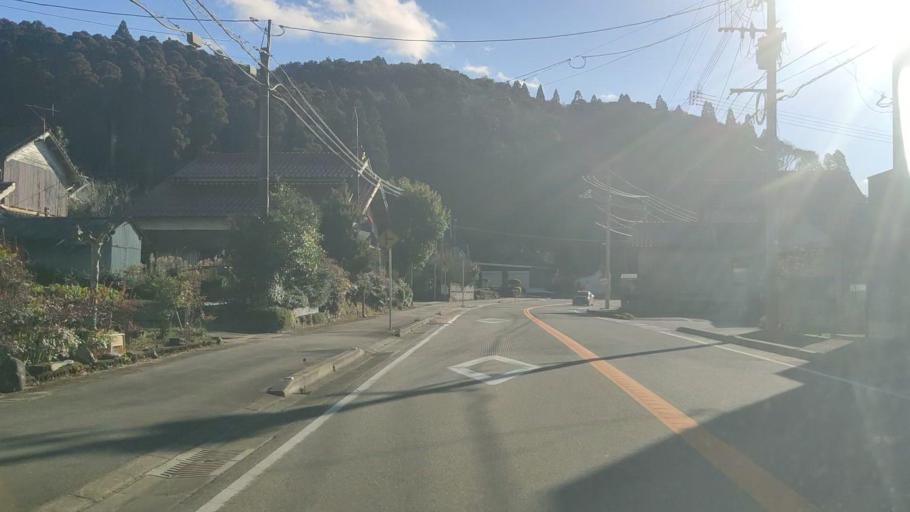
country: JP
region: Fukuoka
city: Maebaru-chuo
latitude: 33.4428
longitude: 130.2689
